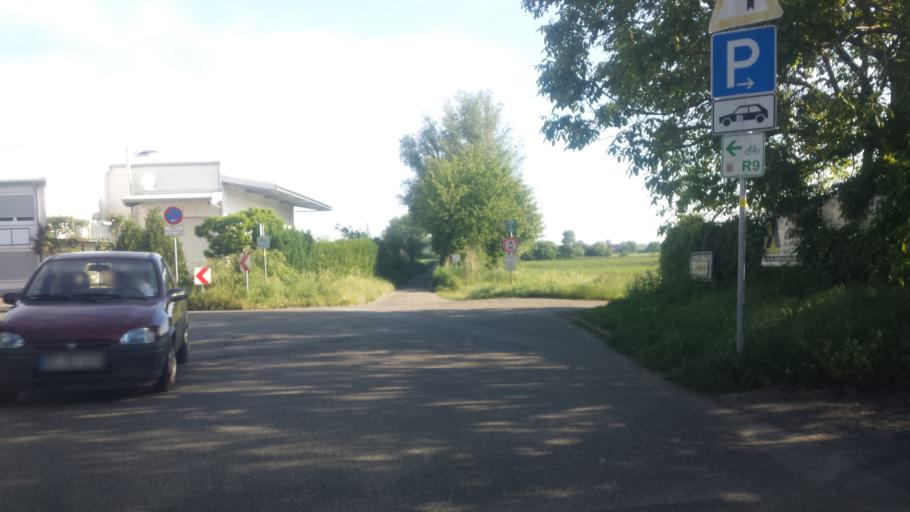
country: DE
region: Hesse
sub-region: Regierungsbezirk Darmstadt
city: Burstadt
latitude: 49.6488
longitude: 8.4706
